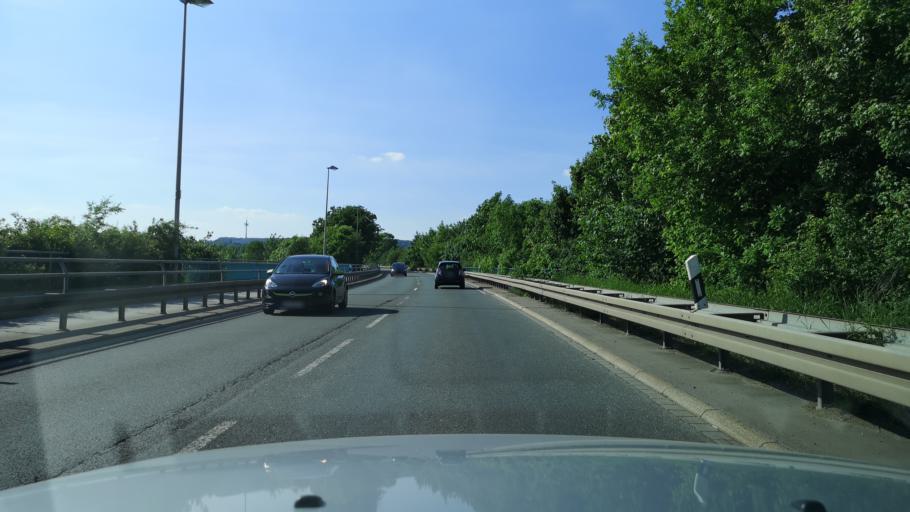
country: DE
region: North Rhine-Westphalia
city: Schwerte
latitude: 51.4376
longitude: 7.5825
